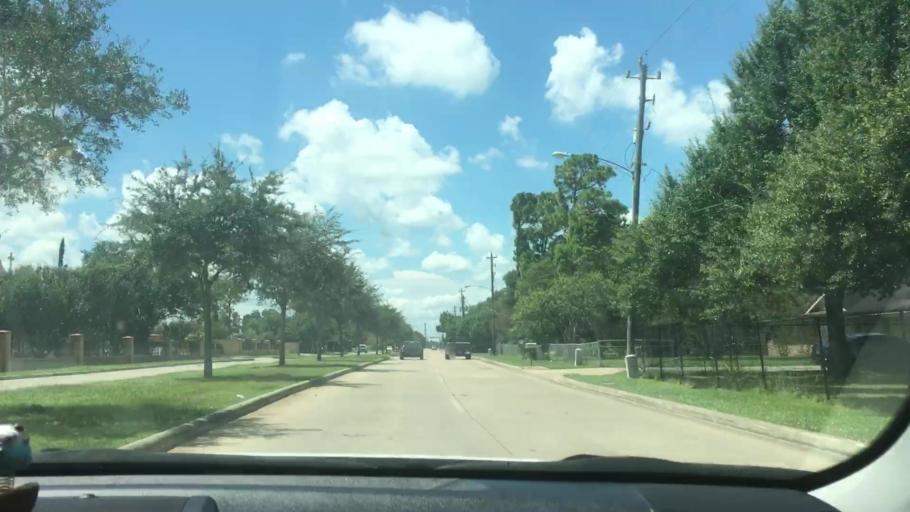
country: US
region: Texas
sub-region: Fort Bend County
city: Fifth Street
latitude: 29.6075
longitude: -95.5457
